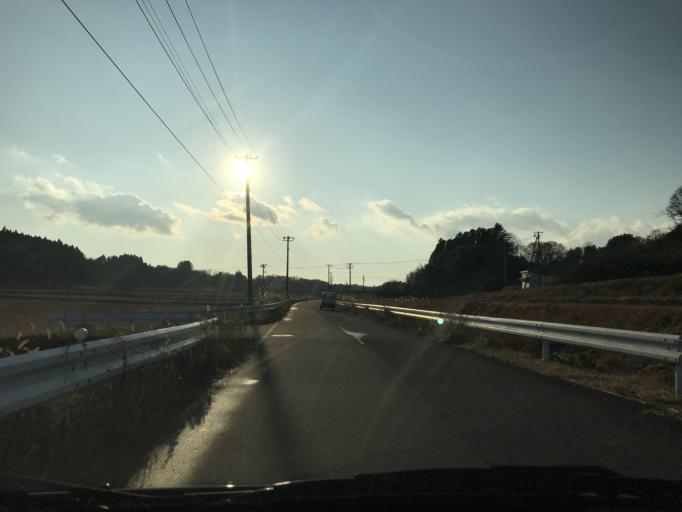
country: JP
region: Miyagi
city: Wakuya
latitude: 38.7026
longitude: 141.1200
